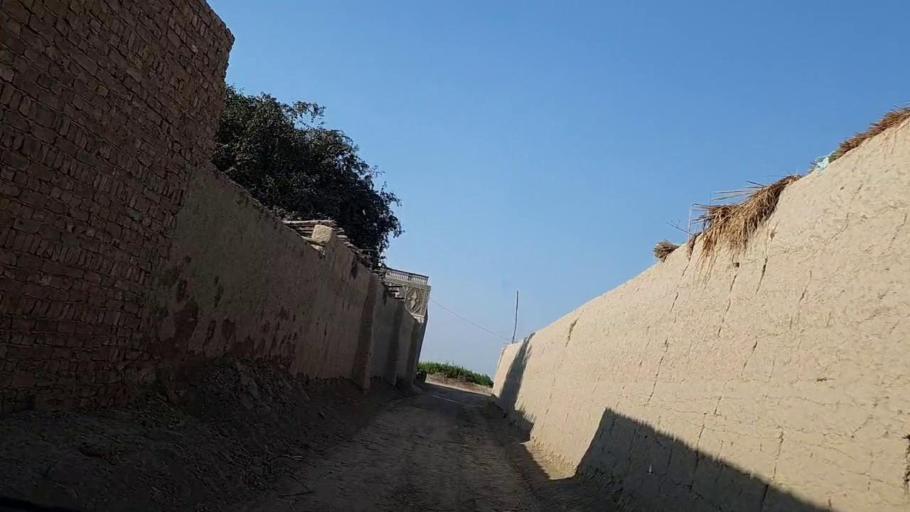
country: PK
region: Sindh
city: Sakrand
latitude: 26.1255
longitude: 68.2371
